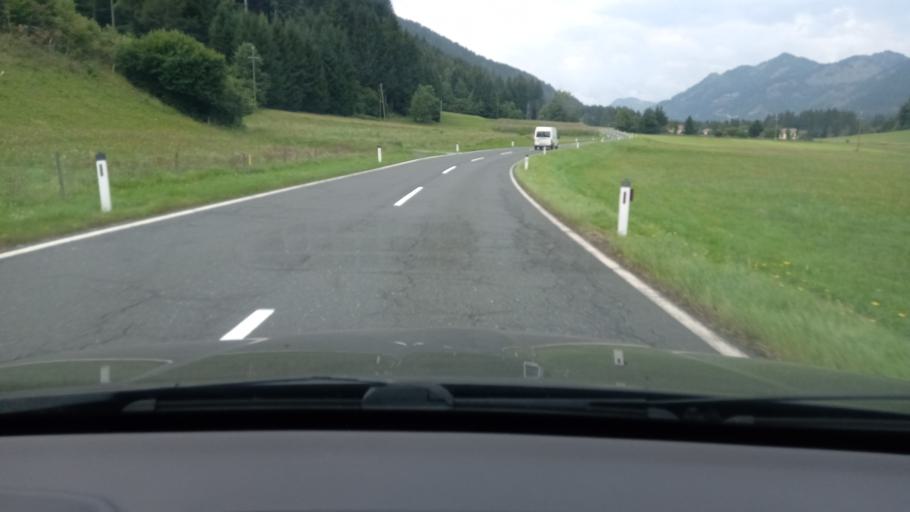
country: AT
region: Carinthia
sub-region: Politischer Bezirk Hermagor
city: Hermagor
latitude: 46.6401
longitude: 13.3443
